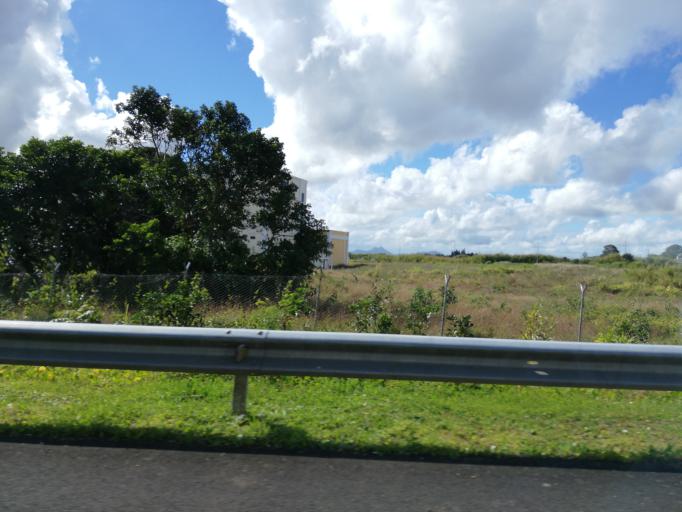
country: MU
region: Moka
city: Quartier Militaire
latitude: -20.2520
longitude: 57.5855
